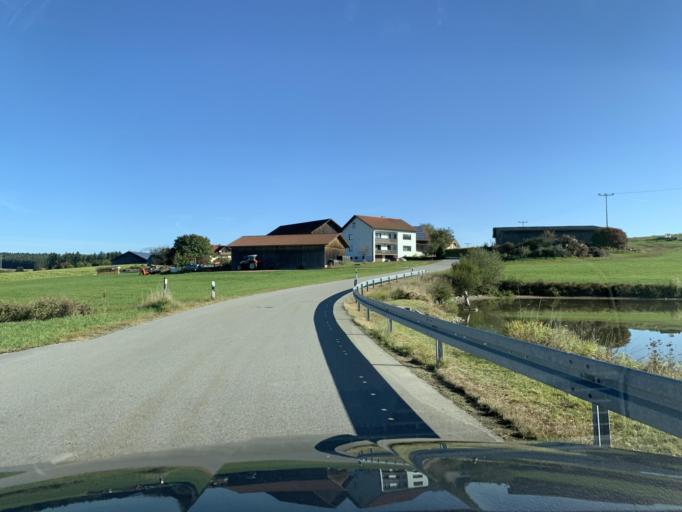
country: DE
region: Bavaria
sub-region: Upper Palatinate
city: Thanstein
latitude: 49.3830
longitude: 12.4786
